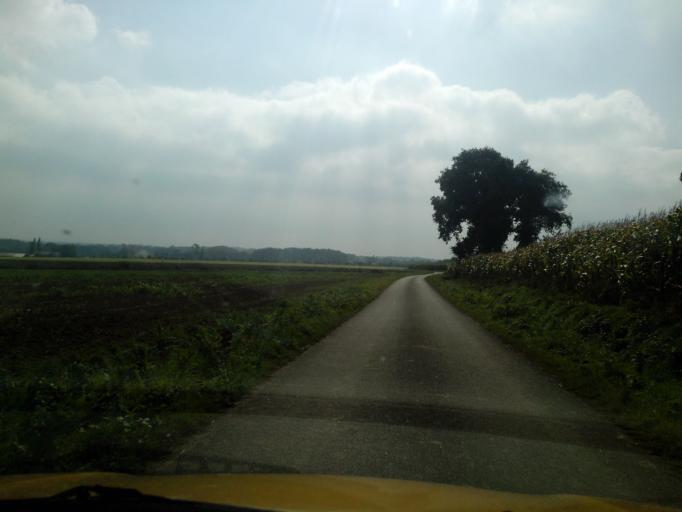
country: FR
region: Brittany
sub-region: Departement du Morbihan
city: Meneac
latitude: 48.1178
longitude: -2.4071
